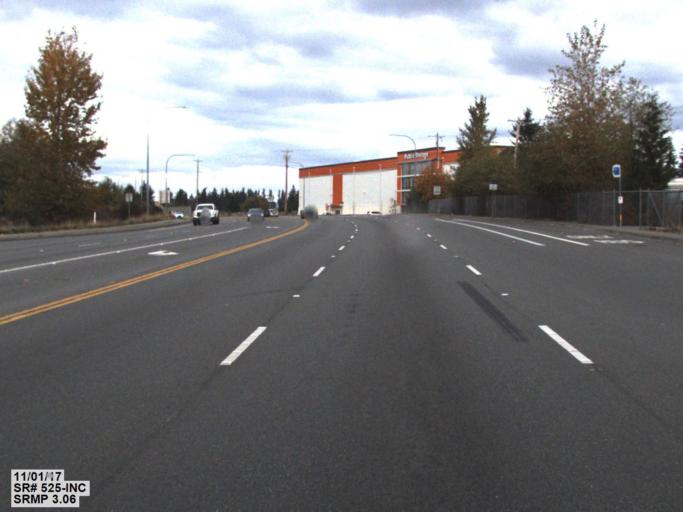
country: US
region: Washington
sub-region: Snohomish County
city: Martha Lake
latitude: 47.8737
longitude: -122.2765
